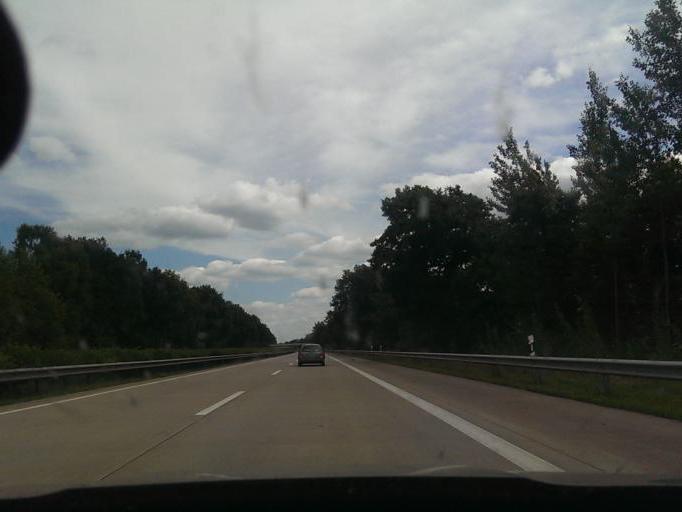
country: DE
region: Lower Saxony
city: Walsrode
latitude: 52.8155
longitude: 9.6195
